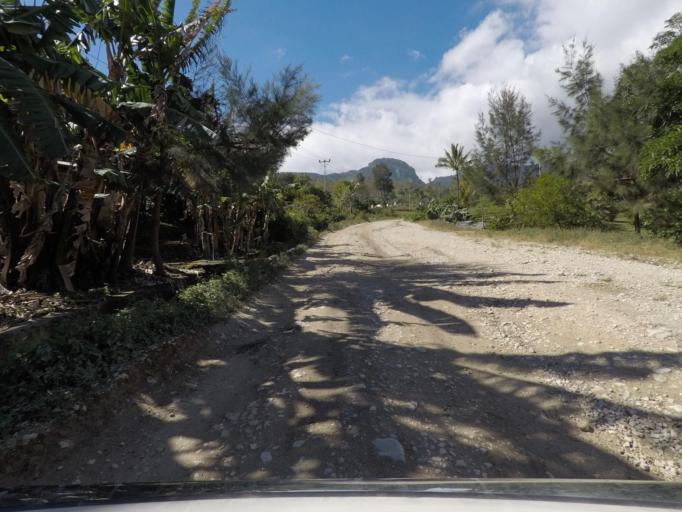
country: TL
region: Baucau
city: Venilale
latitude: -8.6744
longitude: 126.3702
